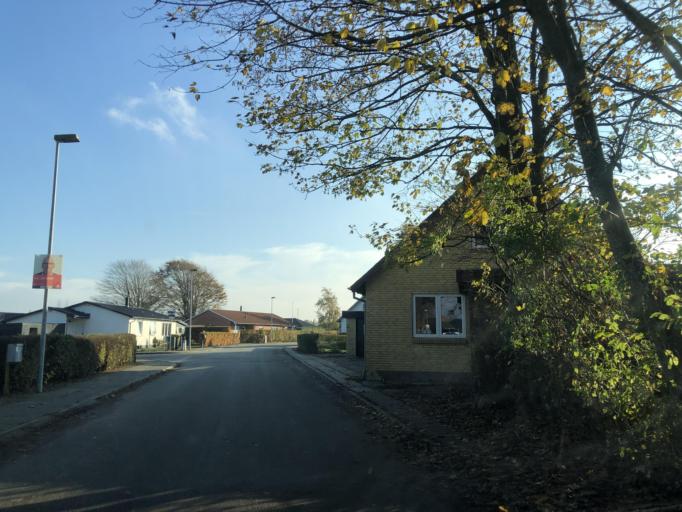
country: DK
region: Central Jutland
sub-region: Holstebro Kommune
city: Vinderup
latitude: 56.4025
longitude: 8.7525
